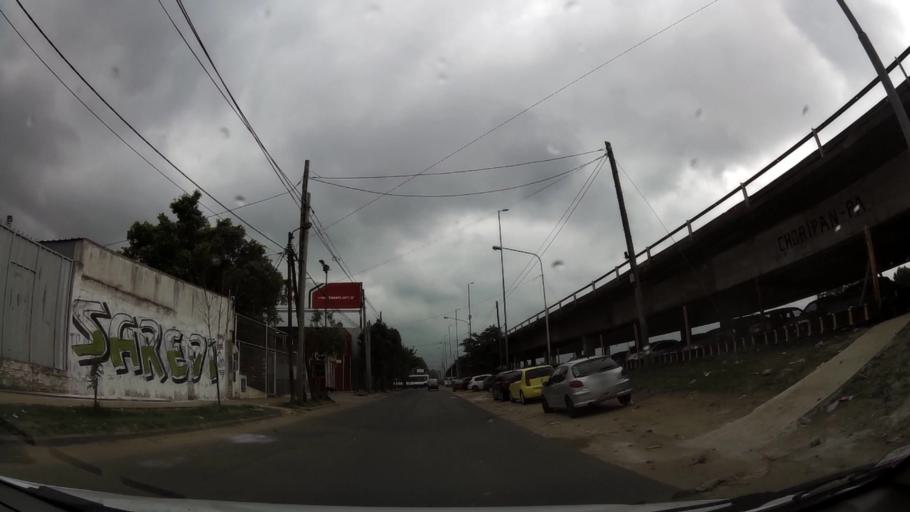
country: AR
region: Buenos Aires
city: San Justo
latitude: -34.7108
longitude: -58.5268
